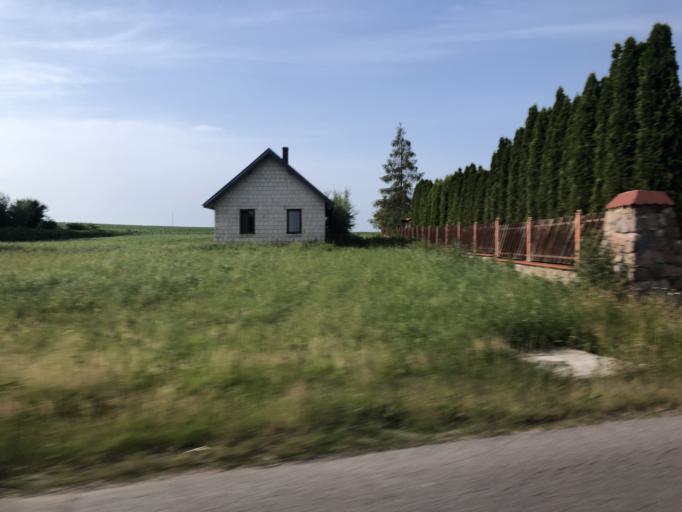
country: PL
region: Podlasie
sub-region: Lomza
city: Lomza
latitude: 53.1539
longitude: 22.0193
